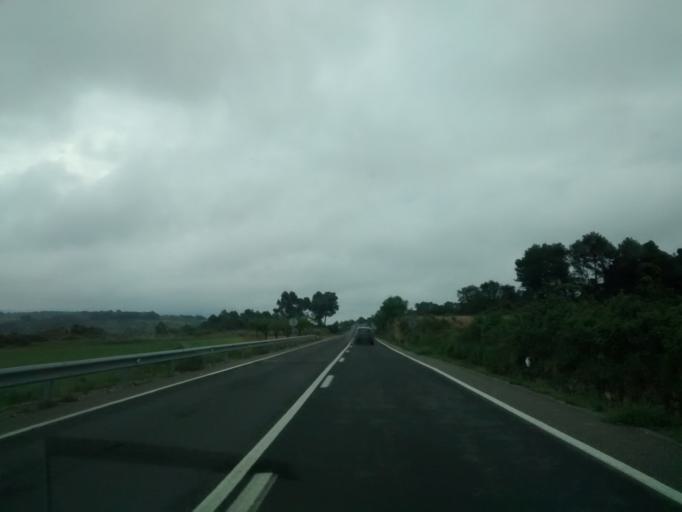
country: ES
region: Catalonia
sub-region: Provincia de Tarragona
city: Bot
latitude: 41.0547
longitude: 0.3612
